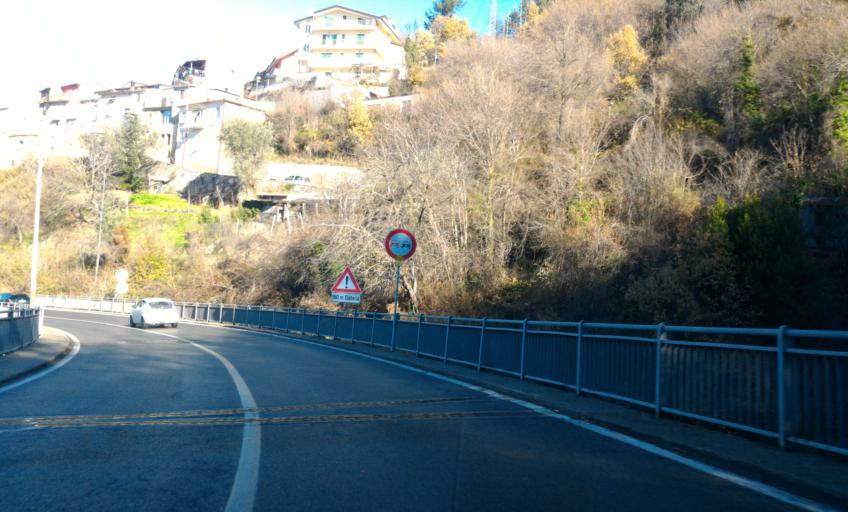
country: IT
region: Calabria
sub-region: Provincia di Cosenza
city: Celico
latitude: 39.3063
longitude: 16.3427
